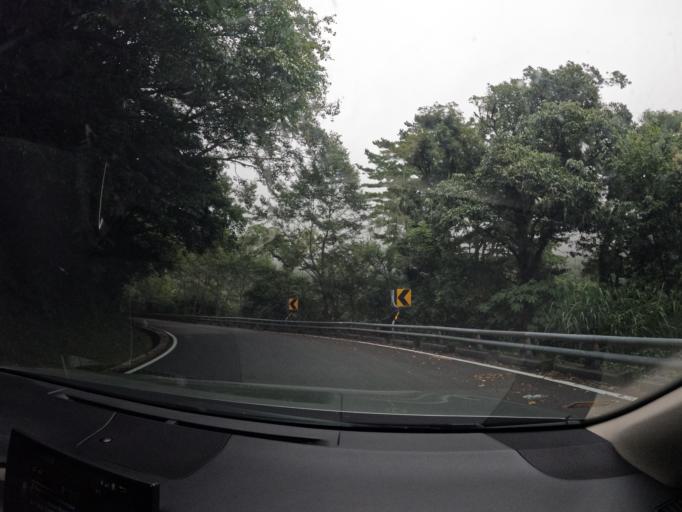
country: TW
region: Taiwan
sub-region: Taitung
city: Taitung
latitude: 23.2441
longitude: 120.9920
